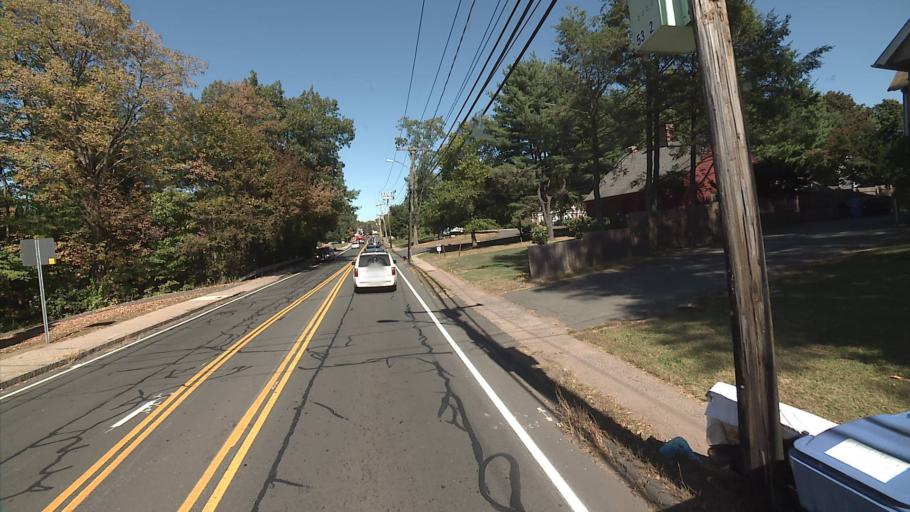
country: US
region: Connecticut
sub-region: Hartford County
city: Manchester
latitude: 41.7990
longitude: -72.5200
